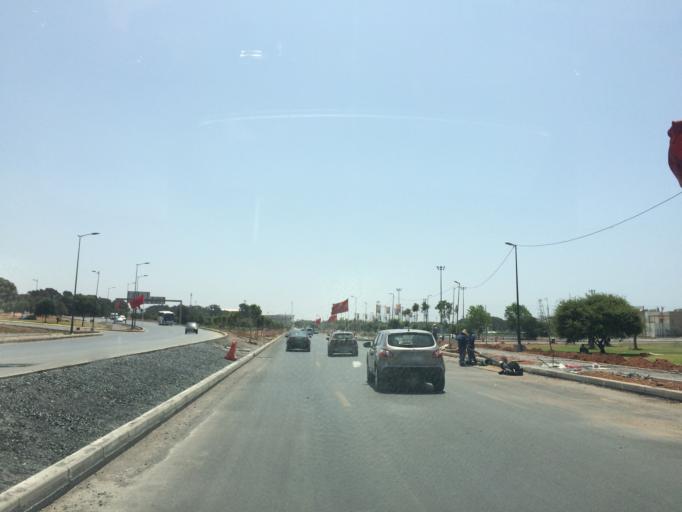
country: MA
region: Rabat-Sale-Zemmour-Zaer
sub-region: Skhirate-Temara
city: Temara
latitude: 33.9724
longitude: -6.8805
